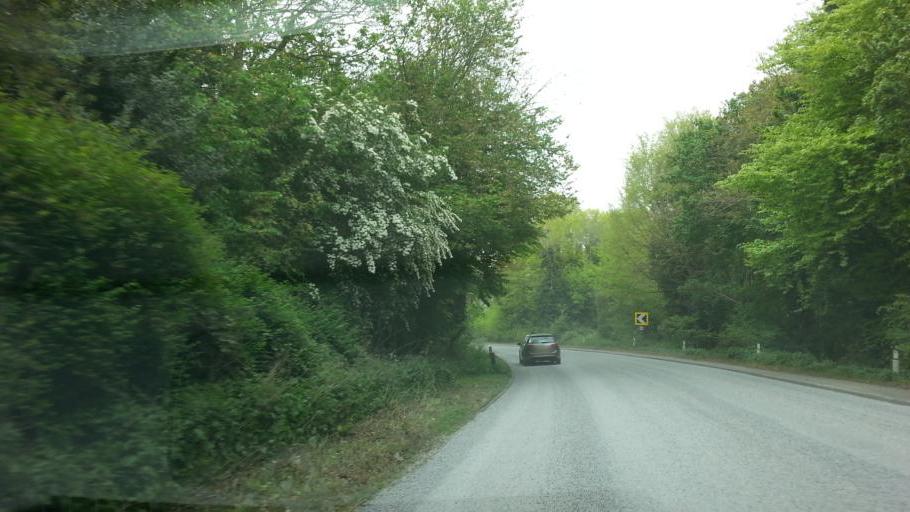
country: GB
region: England
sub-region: Suffolk
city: Bury St Edmunds
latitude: 52.2067
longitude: 0.7550
